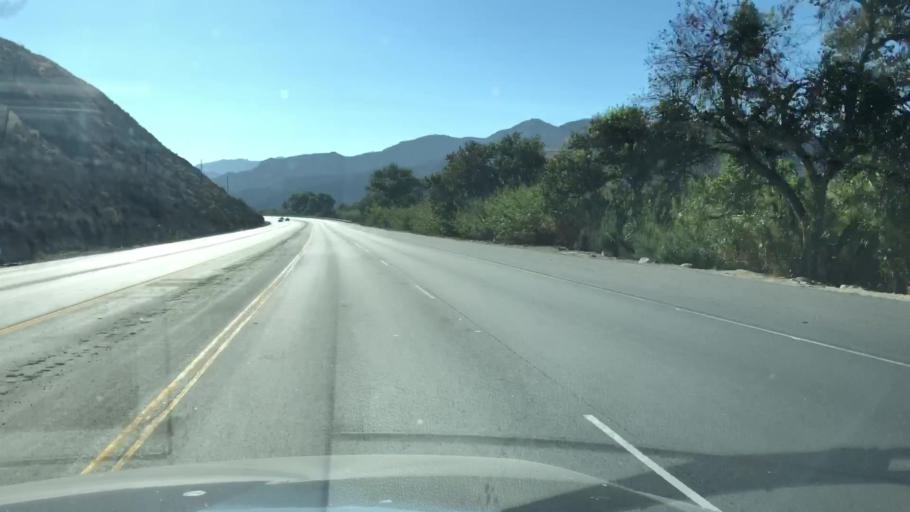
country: US
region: California
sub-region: Ventura County
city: Piru
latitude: 34.4079
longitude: -118.7232
